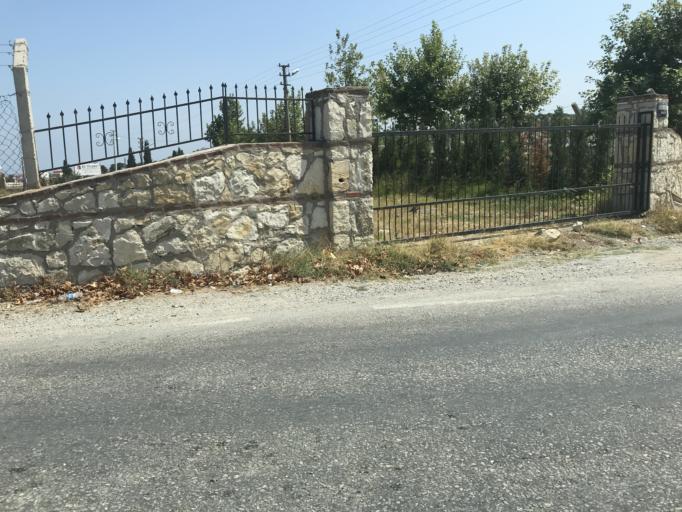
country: TR
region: Izmir
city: Urla
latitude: 38.3156
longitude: 26.7633
